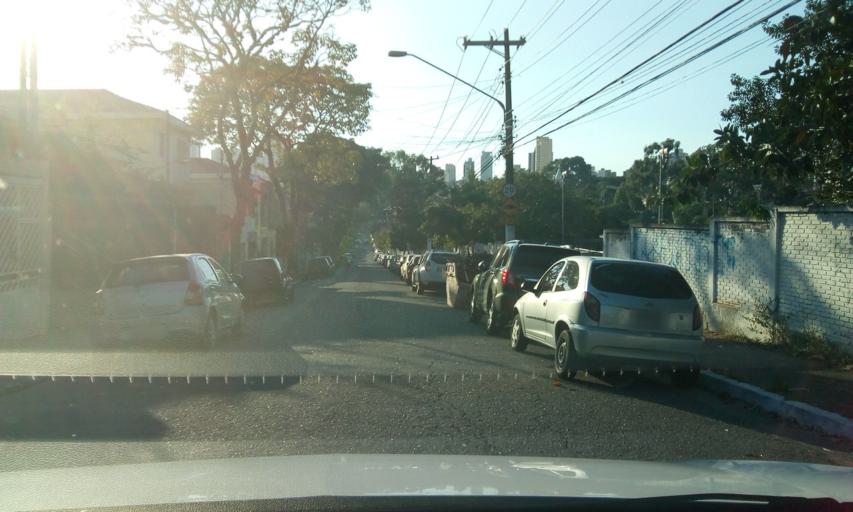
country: BR
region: Sao Paulo
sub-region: Sao Paulo
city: Sao Paulo
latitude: -23.4957
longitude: -46.6144
